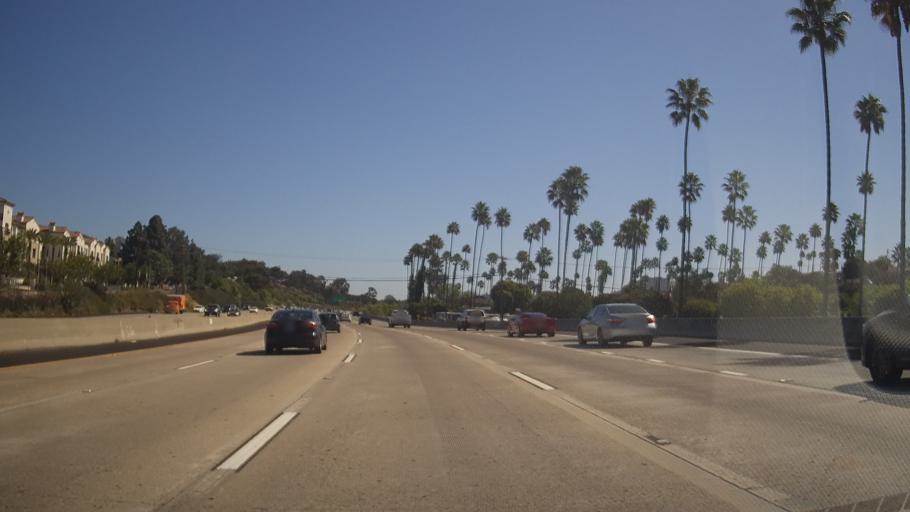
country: US
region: California
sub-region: San Diego County
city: La Mesa
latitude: 32.7726
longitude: -117.0399
